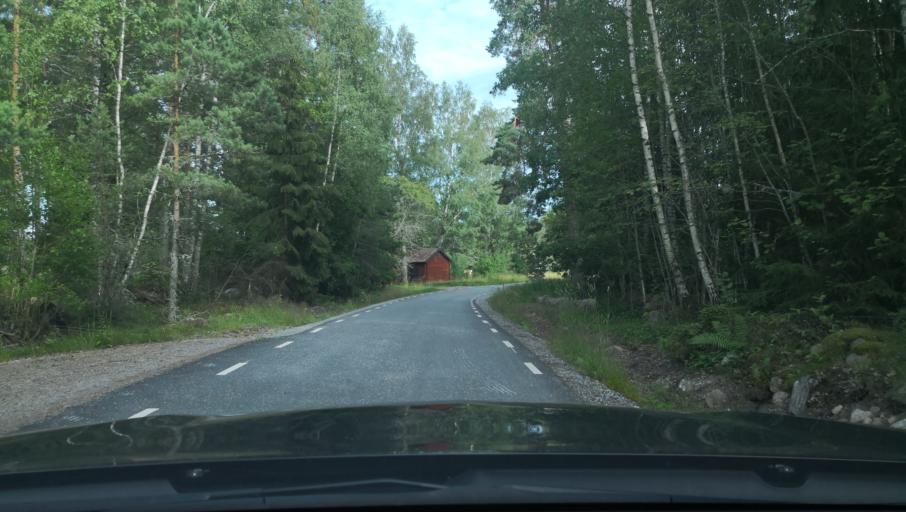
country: SE
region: Vaestmanland
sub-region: Surahammars Kommun
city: Surahammar
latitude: 59.6626
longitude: 16.1729
